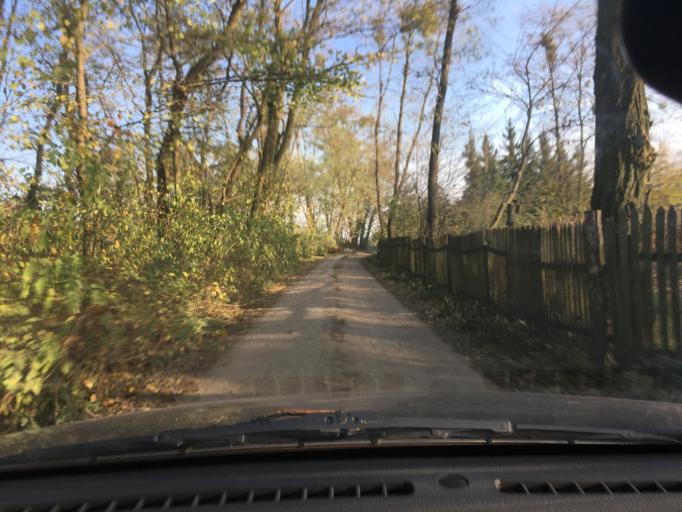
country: PL
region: Masovian Voivodeship
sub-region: Powiat plocki
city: Mala Wies
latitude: 52.4422
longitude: 20.1130
